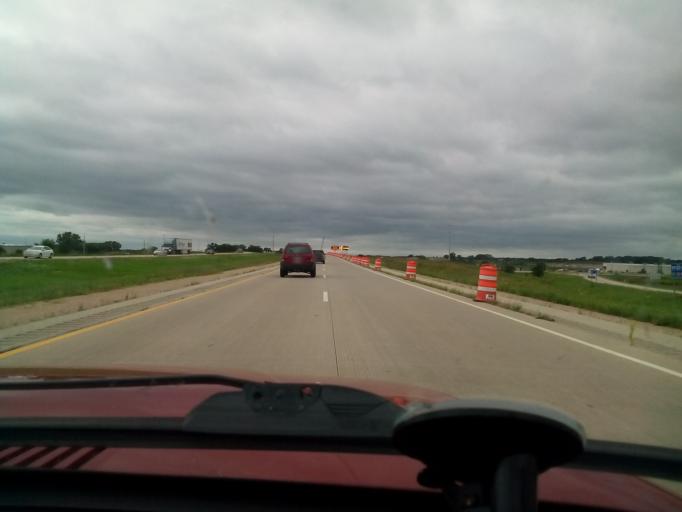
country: US
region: Wisconsin
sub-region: Columbia County
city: Columbus
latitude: 43.3496
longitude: -89.0317
